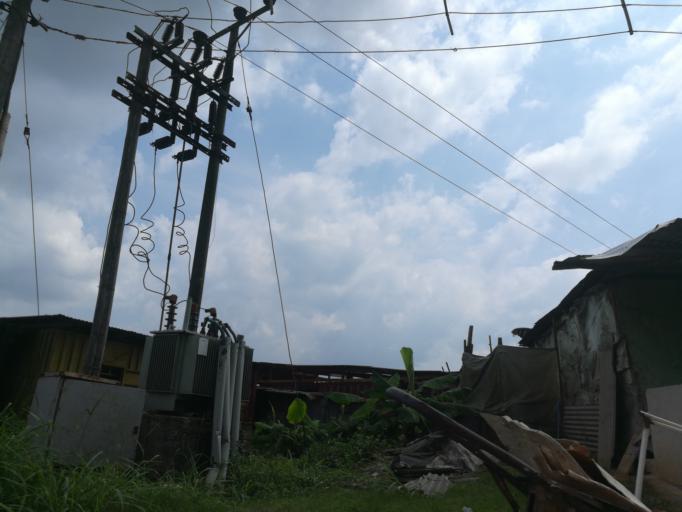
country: NG
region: Rivers
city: Okrika
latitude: 4.7345
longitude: 7.1533
